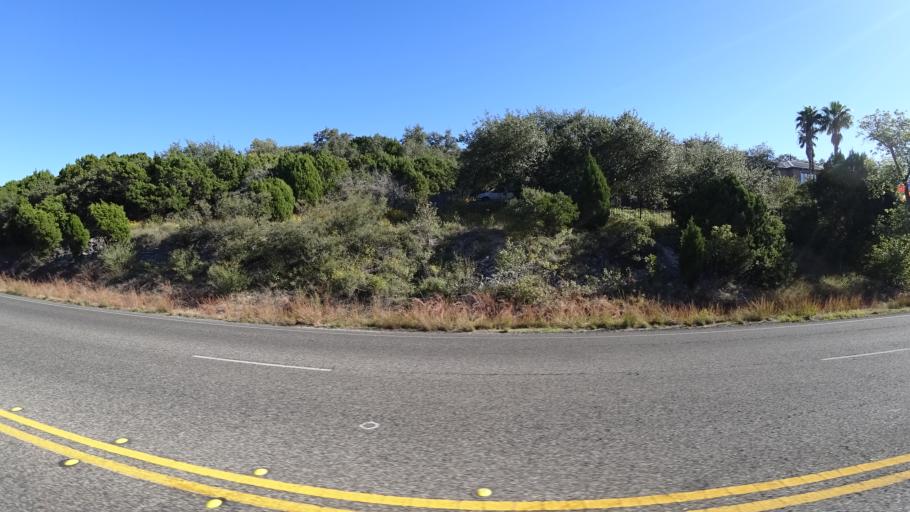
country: US
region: Texas
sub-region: Travis County
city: West Lake Hills
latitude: 30.3436
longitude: -97.7849
